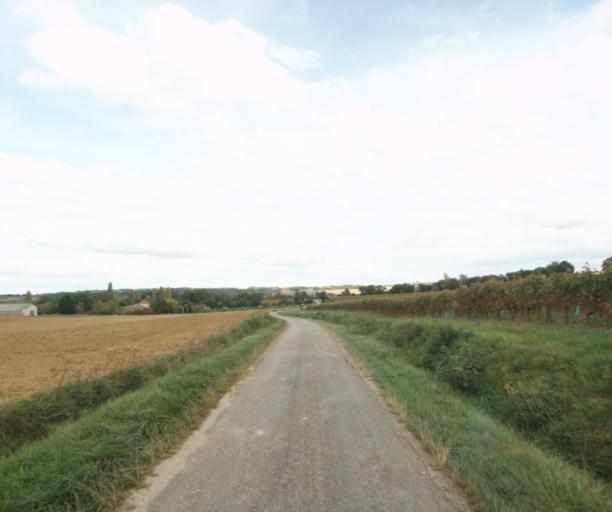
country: FR
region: Midi-Pyrenees
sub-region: Departement du Gers
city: Gondrin
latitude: 43.8614
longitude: 0.2641
